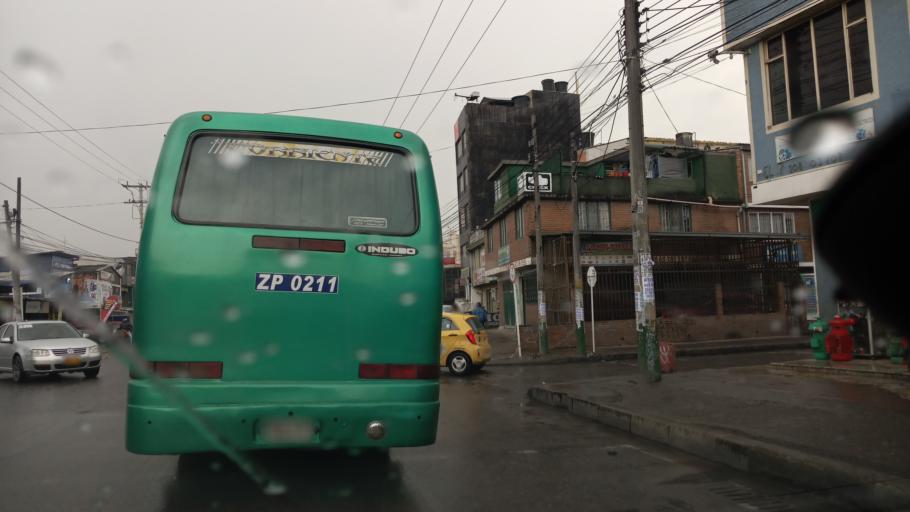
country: CO
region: Cundinamarca
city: Funza
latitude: 4.6784
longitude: -74.1502
